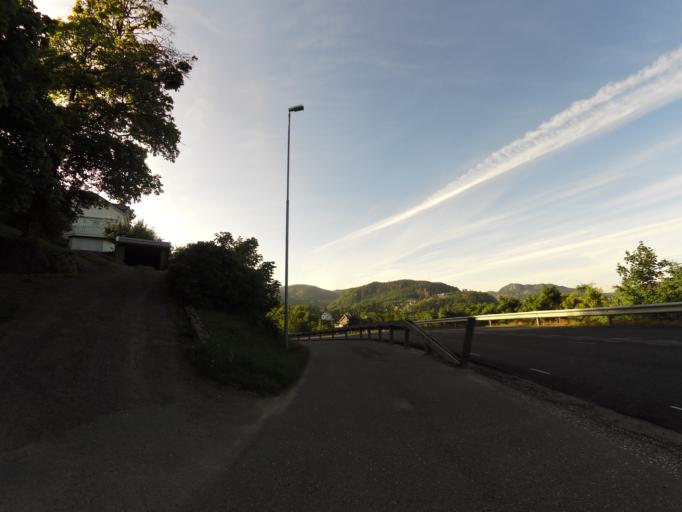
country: NO
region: Vest-Agder
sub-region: Flekkefjord
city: Flekkefjord
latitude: 58.2876
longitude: 6.6500
